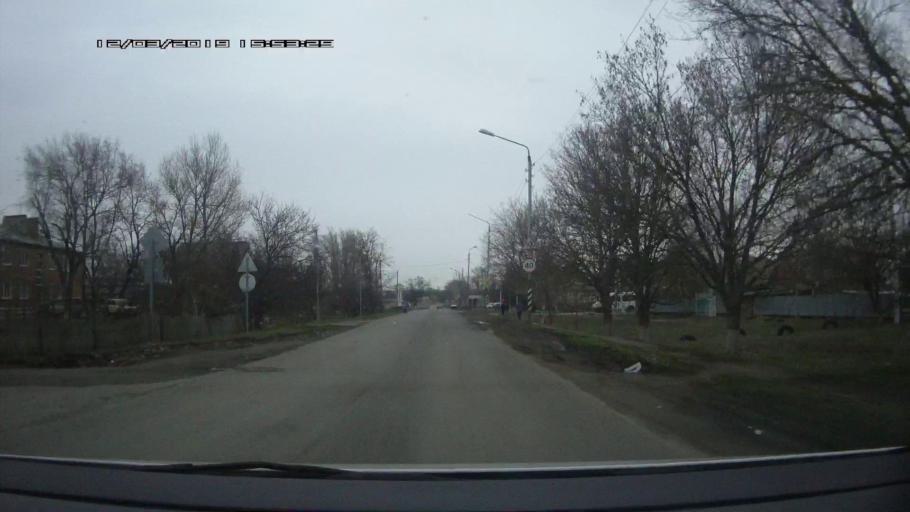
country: RU
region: Rostov
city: Novobataysk
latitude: 46.8853
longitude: 39.7762
